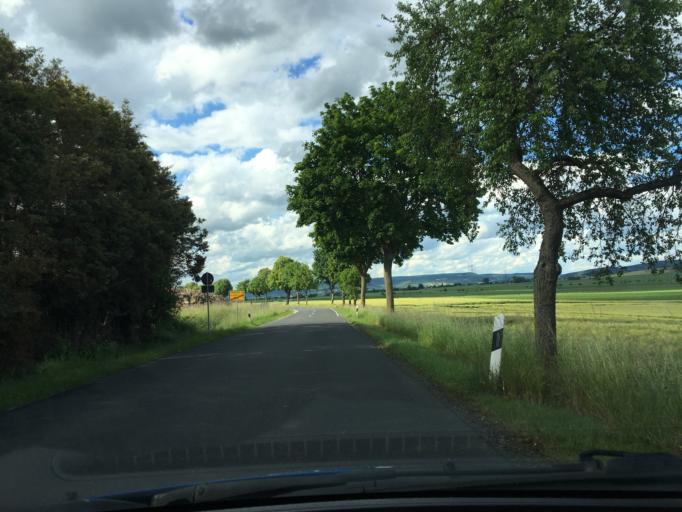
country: DE
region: Lower Saxony
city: Moringen
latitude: 51.7430
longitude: 9.8796
